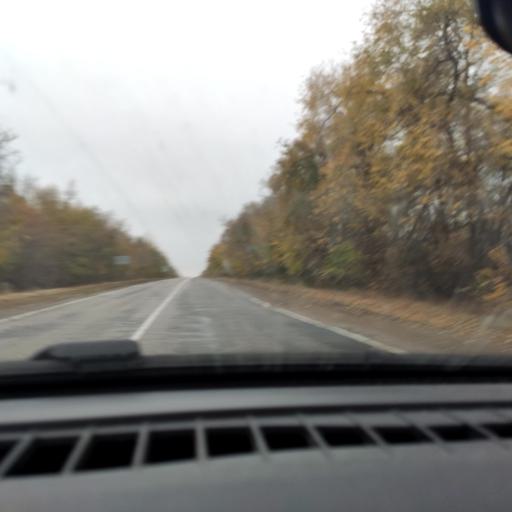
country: RU
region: Voronezj
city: Uryv-Pokrovka
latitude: 51.1437
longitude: 39.0570
